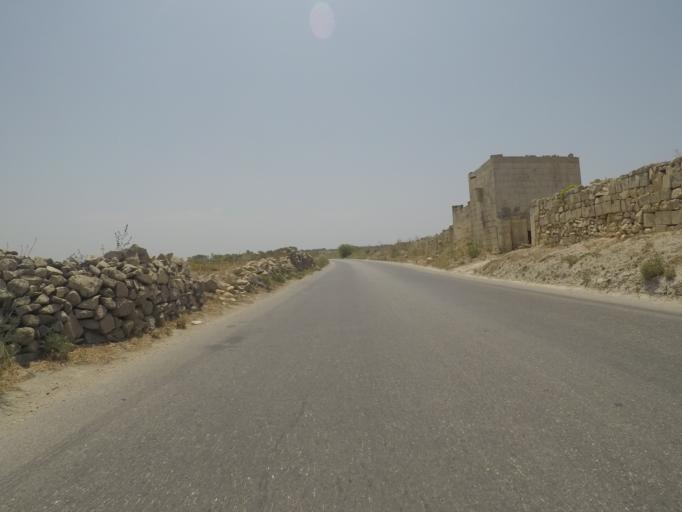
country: MT
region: Is-Siggiewi
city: Siggiewi
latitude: 35.8649
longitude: 14.4175
